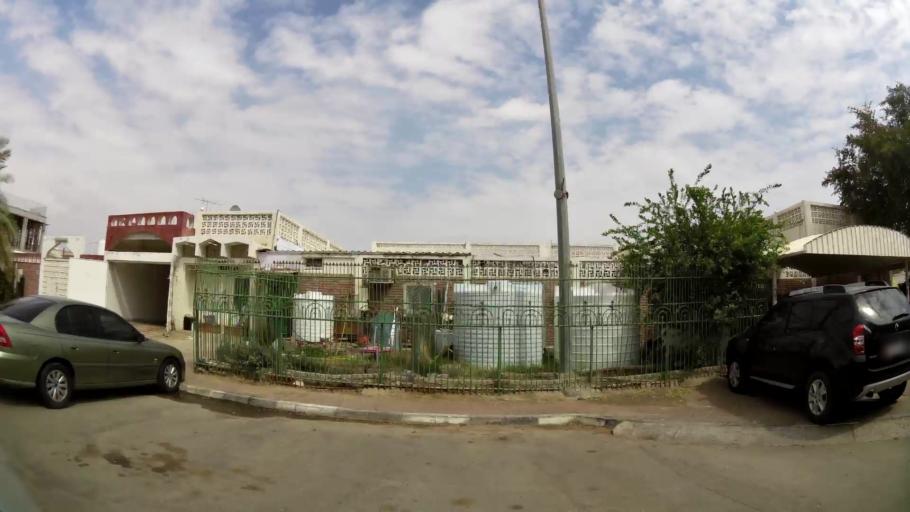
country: AE
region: Abu Dhabi
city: Al Ain
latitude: 24.1989
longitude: 55.7937
